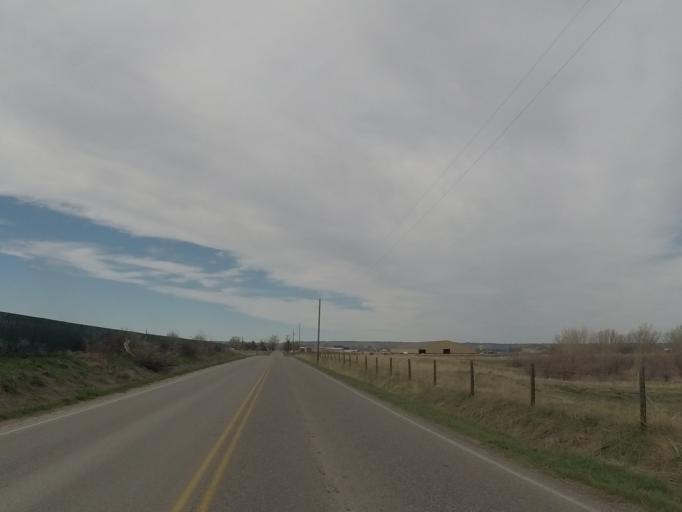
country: US
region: Montana
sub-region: Yellowstone County
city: Laurel
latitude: 45.7155
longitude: -108.6587
